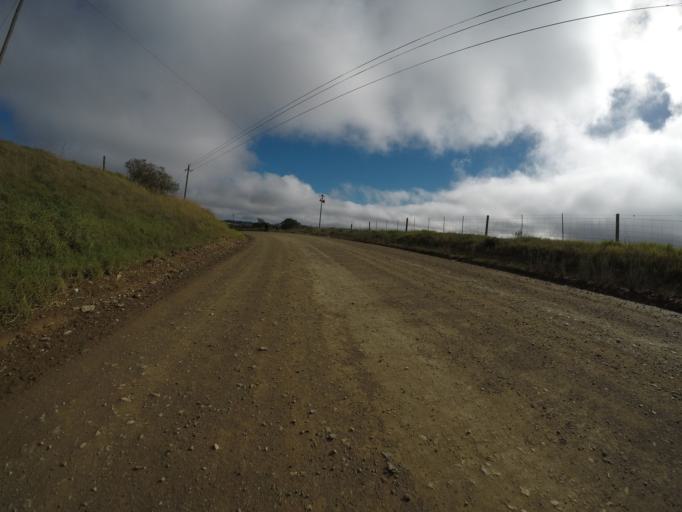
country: ZA
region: Western Cape
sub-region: Cape Winelands District Municipality
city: Ashton
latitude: -34.1305
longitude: 19.8532
